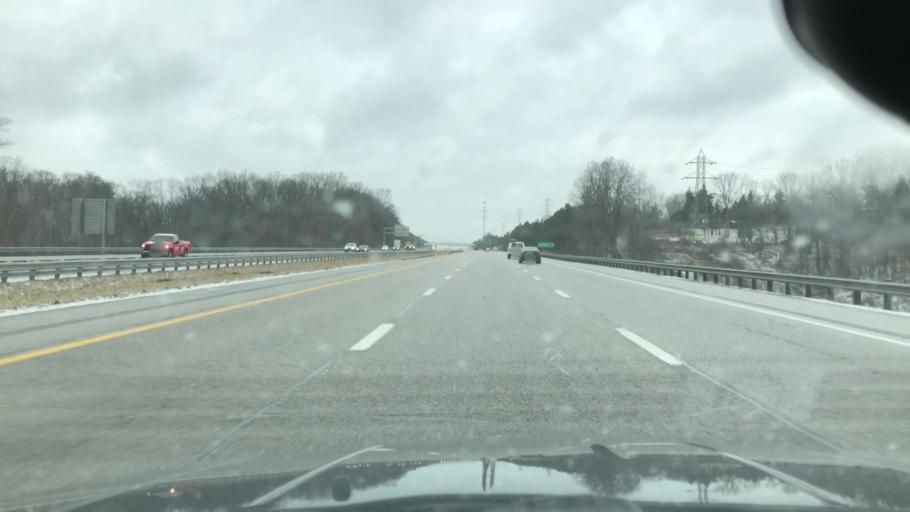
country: US
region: Ohio
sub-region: Cuyahoga County
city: Brecksville
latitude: 41.3272
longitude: -81.6488
